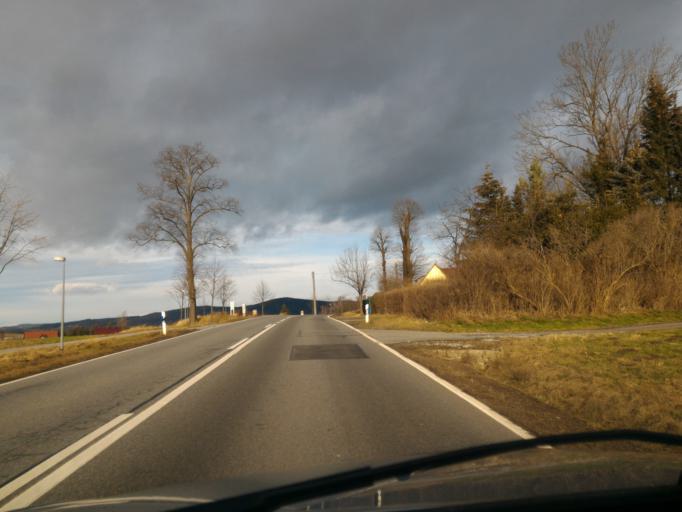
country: DE
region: Saxony
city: Oppach
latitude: 51.0466
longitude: 14.5125
